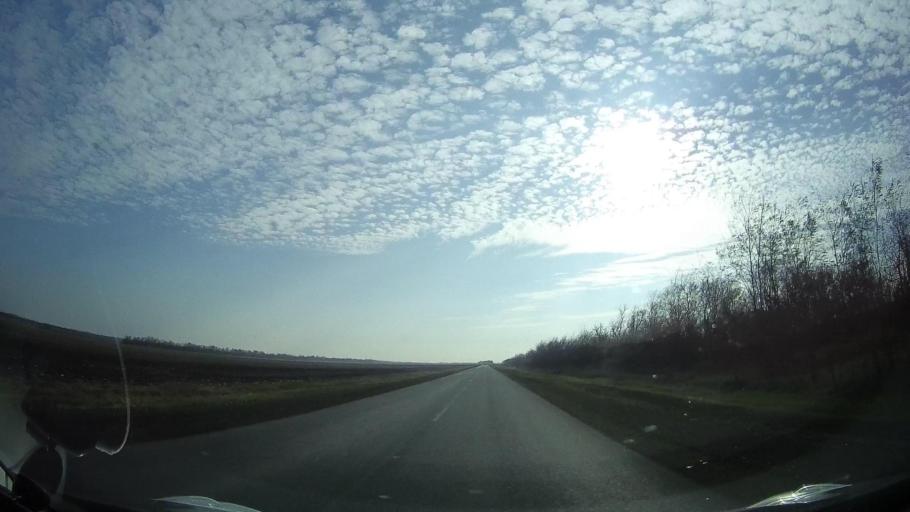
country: RU
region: Rostov
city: Veselyy
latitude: 46.9745
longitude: 40.7198
